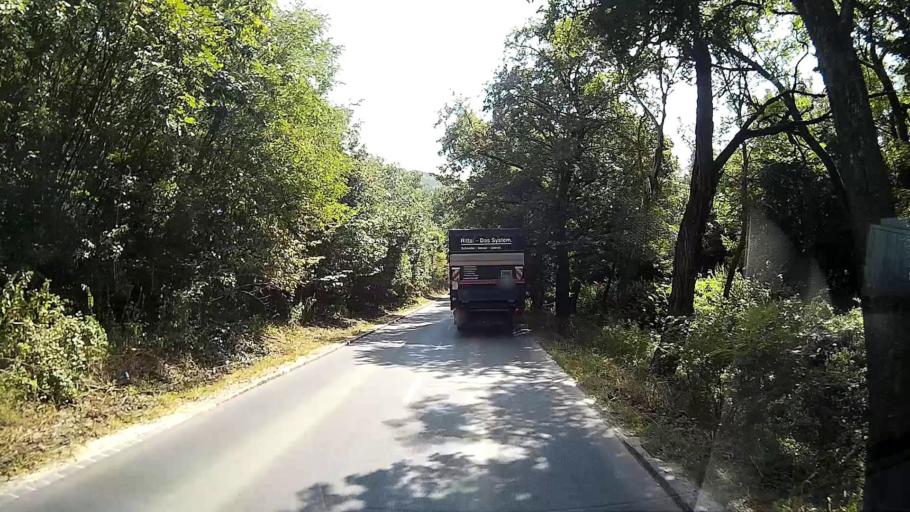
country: HU
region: Pest
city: Budakeszi
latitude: 47.5380
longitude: 18.9473
